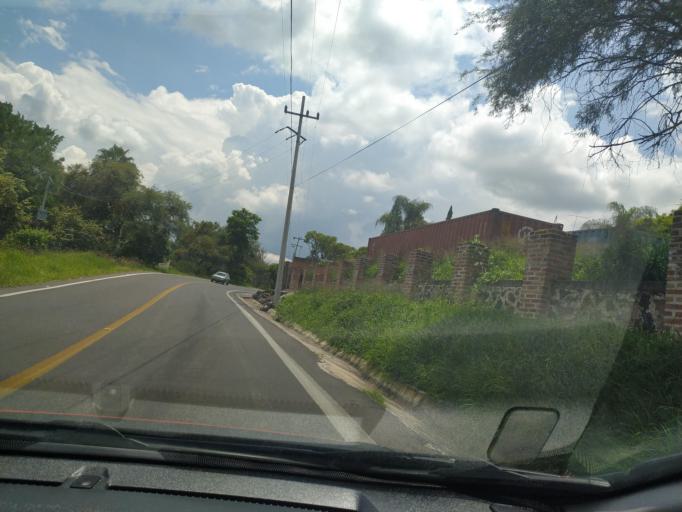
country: MX
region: Jalisco
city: Villa Corona
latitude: 20.4111
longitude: -103.6792
